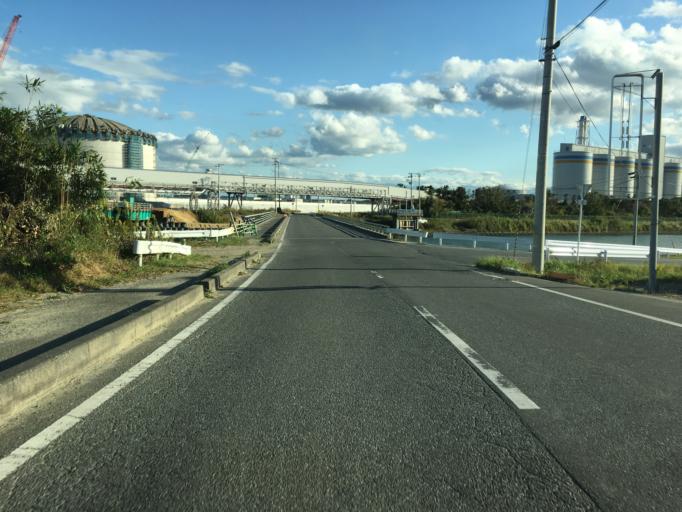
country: JP
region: Miyagi
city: Marumori
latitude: 37.8530
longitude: 140.9458
